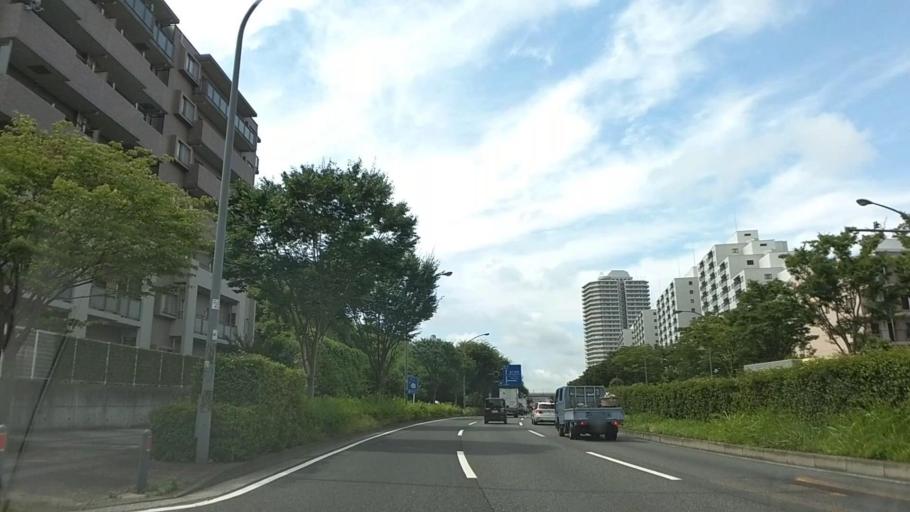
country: JP
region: Kanagawa
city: Yokohama
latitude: 35.4342
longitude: 139.5635
